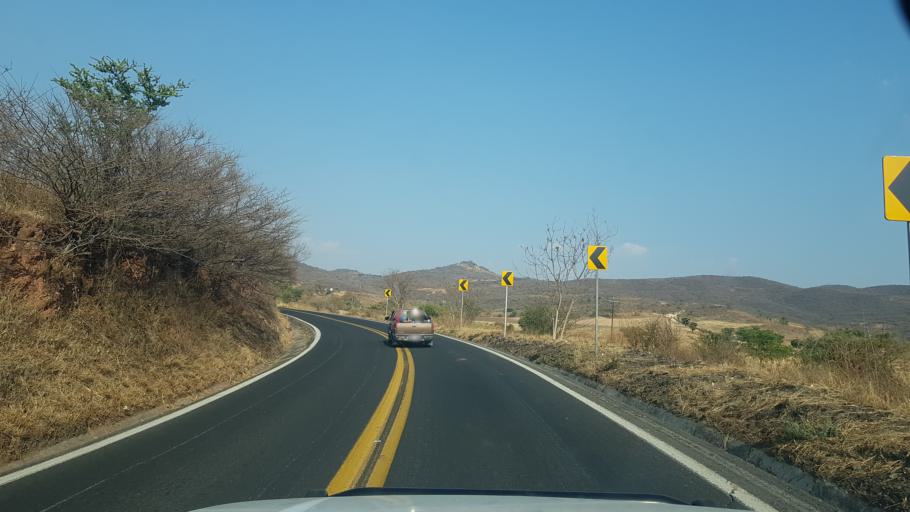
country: MX
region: Puebla
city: Calmeca
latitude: 18.6416
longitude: -98.6189
